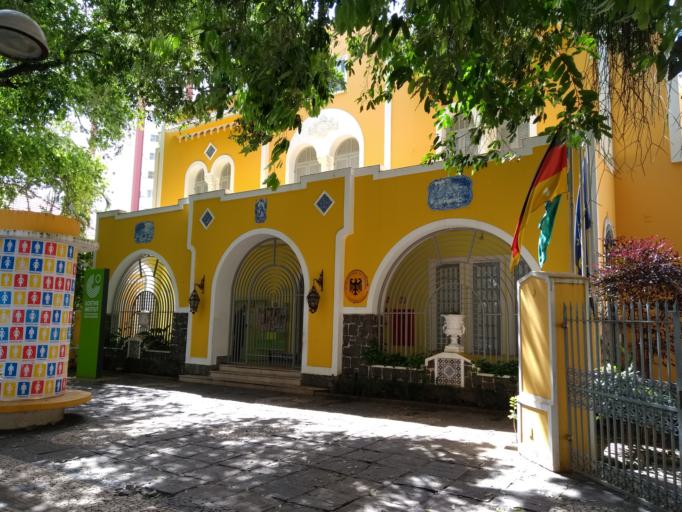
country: BR
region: Bahia
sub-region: Salvador
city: Salvador
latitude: -12.9895
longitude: -38.5239
